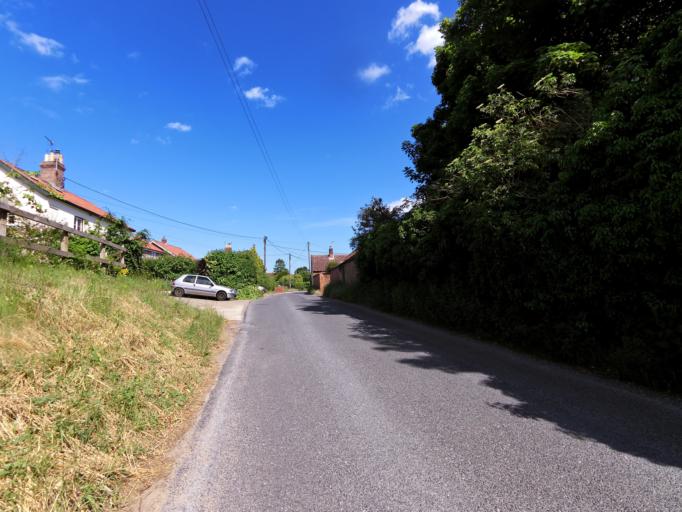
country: GB
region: England
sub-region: Suffolk
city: Shotley Gate
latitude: 52.0063
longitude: 1.2506
